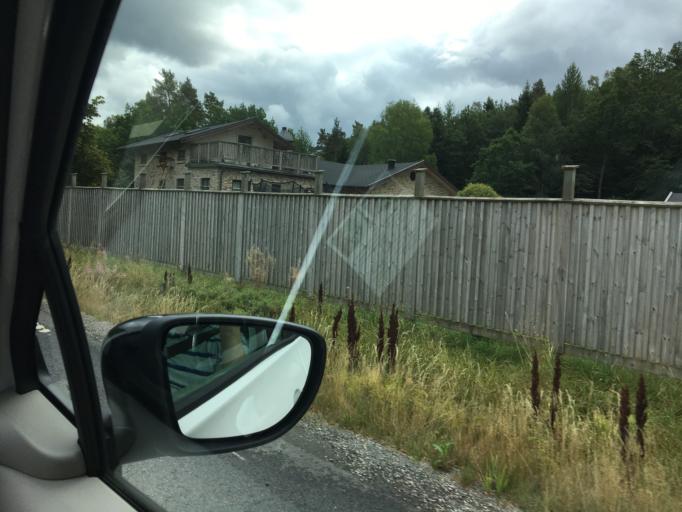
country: SE
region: Vaestra Goetaland
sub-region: Ale Kommun
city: Nodinge-Nol
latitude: 57.8844
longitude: 12.0812
